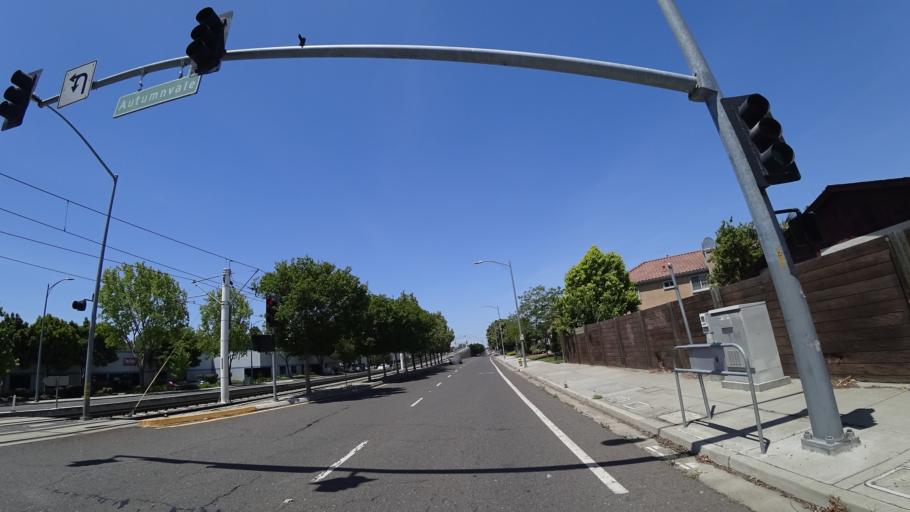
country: US
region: California
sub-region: Santa Clara County
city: Milpitas
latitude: 37.4049
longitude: -121.8845
